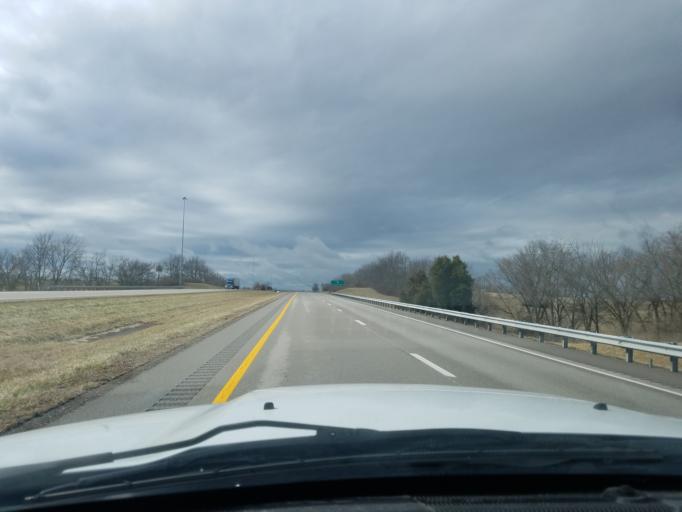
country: US
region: Kentucky
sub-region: Montgomery County
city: Mount Sterling
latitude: 38.0897
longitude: -83.8903
